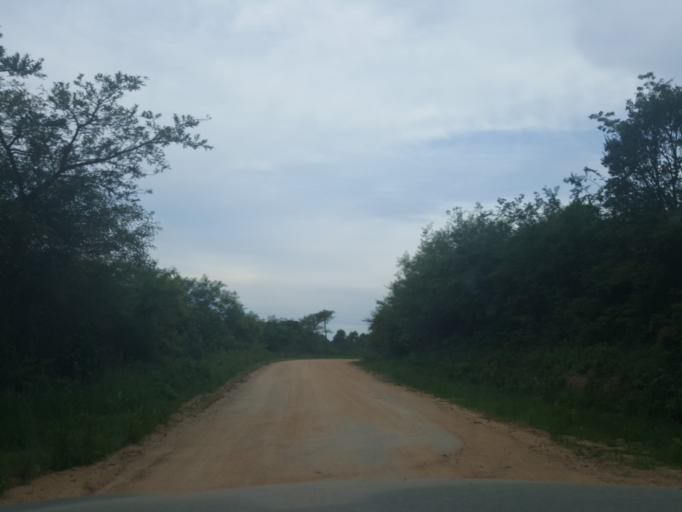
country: ZA
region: Limpopo
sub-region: Mopani District Municipality
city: Hoedspruit
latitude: -24.5974
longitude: 30.9205
